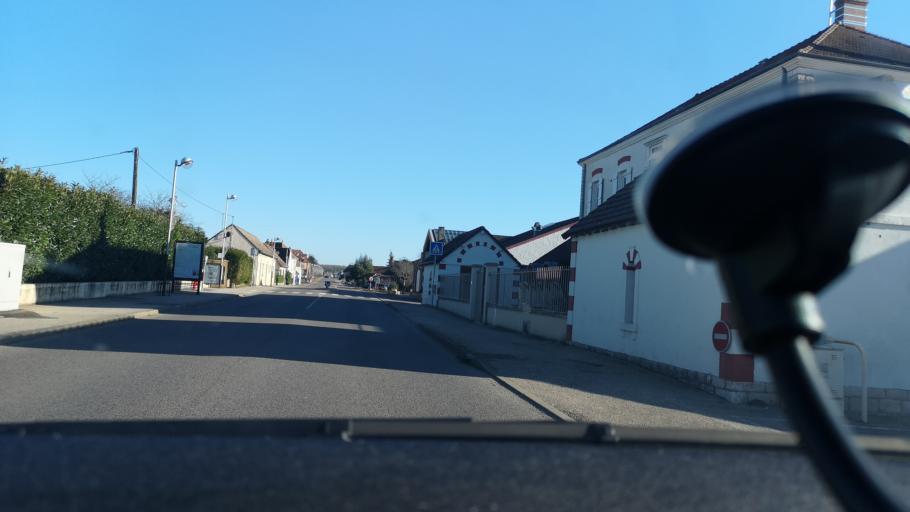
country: FR
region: Bourgogne
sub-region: Departement de Saone-et-Loire
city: Saint-Marcel
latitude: 46.7833
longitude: 4.9189
